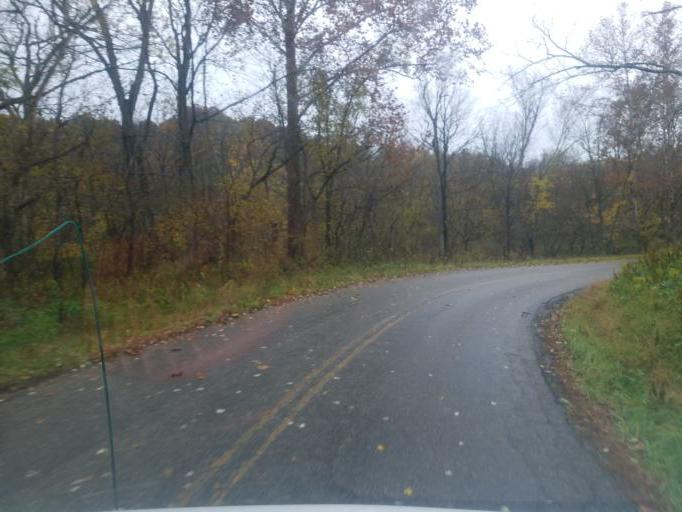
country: US
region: Ohio
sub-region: Washington County
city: Beverly
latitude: 39.4572
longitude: -81.7816
